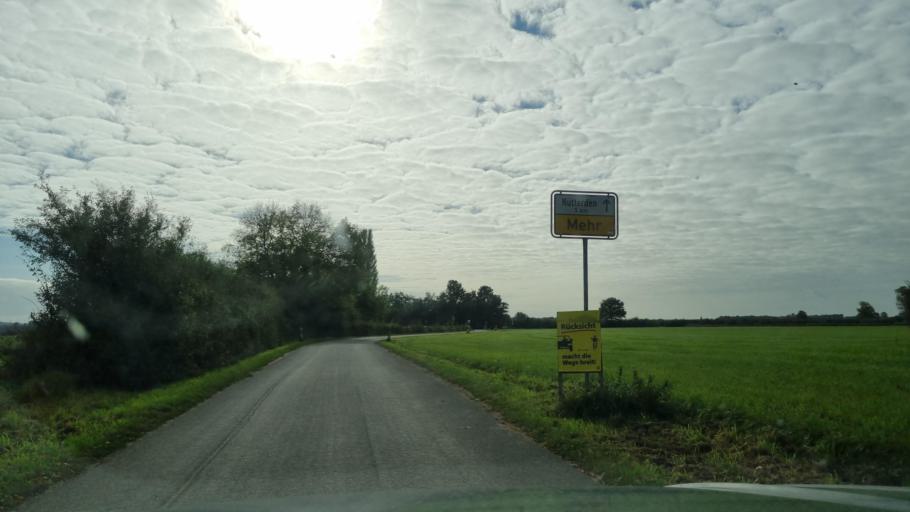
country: DE
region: North Rhine-Westphalia
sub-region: Regierungsbezirk Dusseldorf
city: Kranenburg
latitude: 51.8095
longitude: 6.0535
